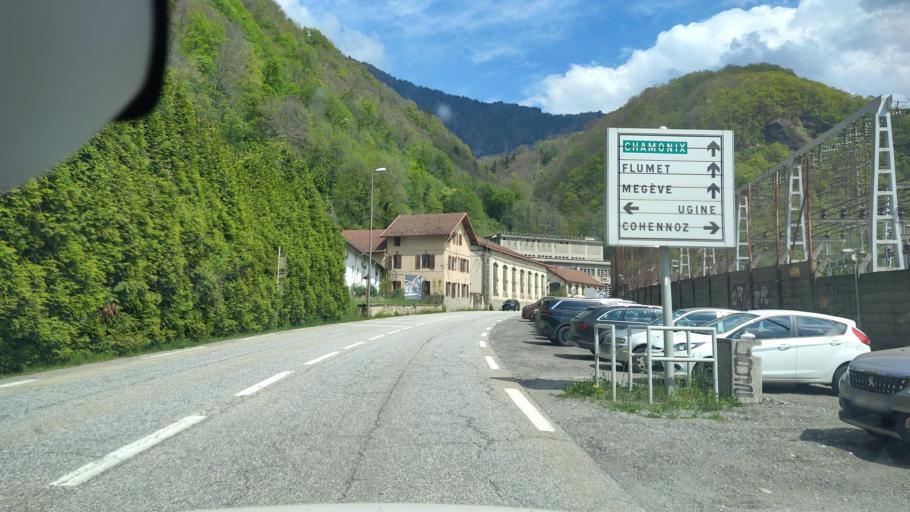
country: FR
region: Rhone-Alpes
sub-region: Departement de la Savoie
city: Ugine
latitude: 45.7505
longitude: 6.4324
